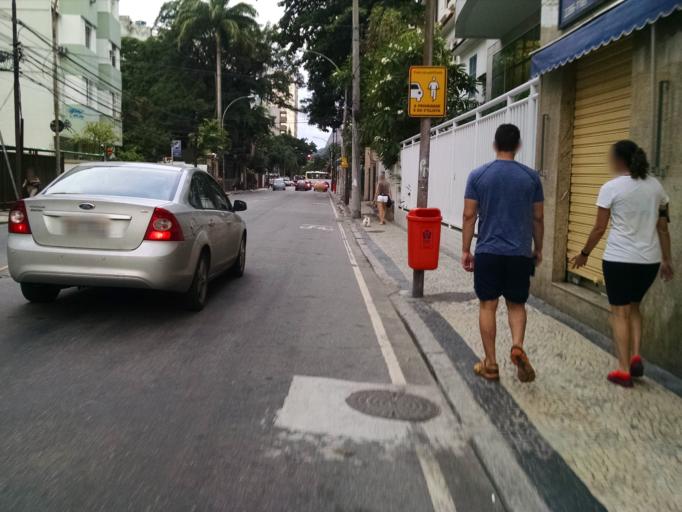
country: BR
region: Rio de Janeiro
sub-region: Rio De Janeiro
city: Rio de Janeiro
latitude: -22.9437
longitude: -43.1851
